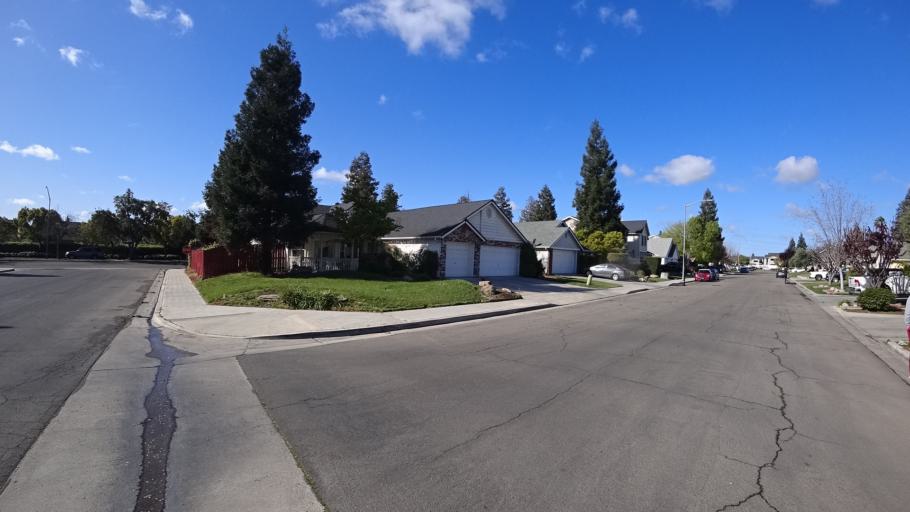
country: US
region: California
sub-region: Fresno County
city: West Park
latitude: 36.8225
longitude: -119.8781
